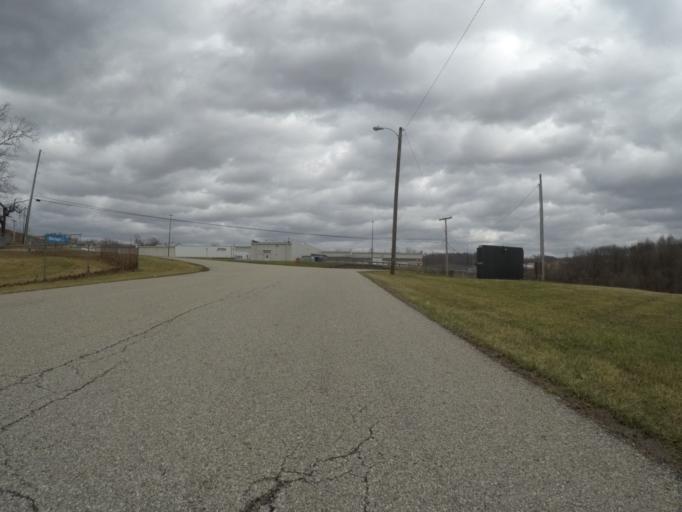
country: US
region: West Virginia
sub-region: Cabell County
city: Pea Ridge
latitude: 38.4056
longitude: -82.3741
